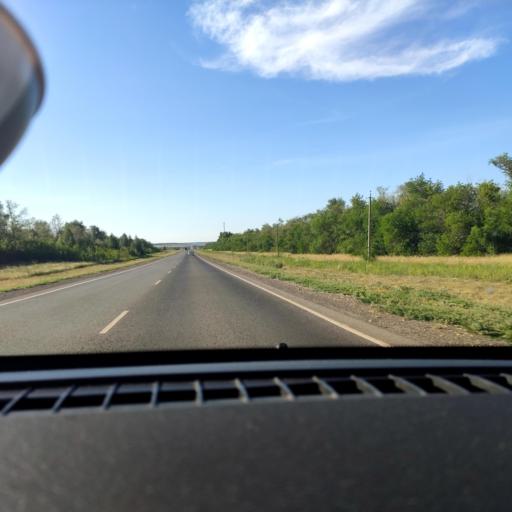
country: RU
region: Samara
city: Krasnoarmeyskoye
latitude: 52.8786
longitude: 49.9803
